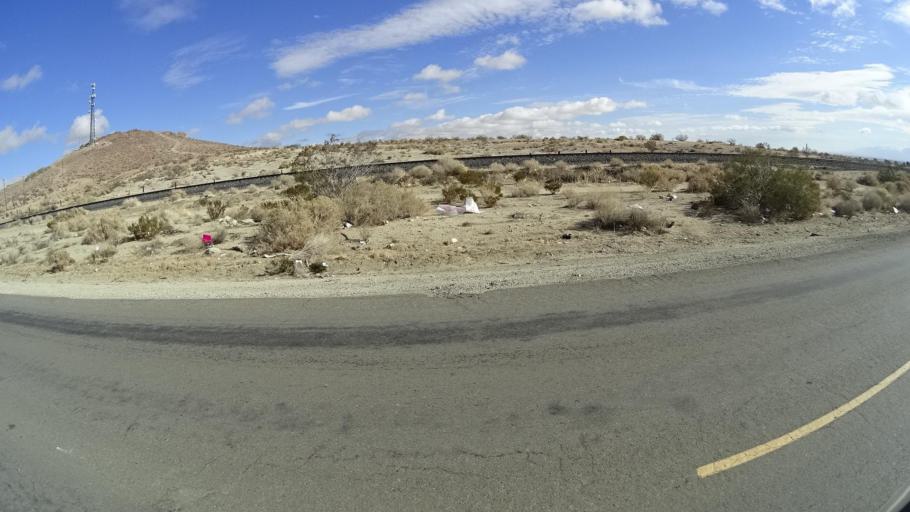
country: US
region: California
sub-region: Kern County
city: Rosamond
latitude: 34.8776
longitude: -118.1653
